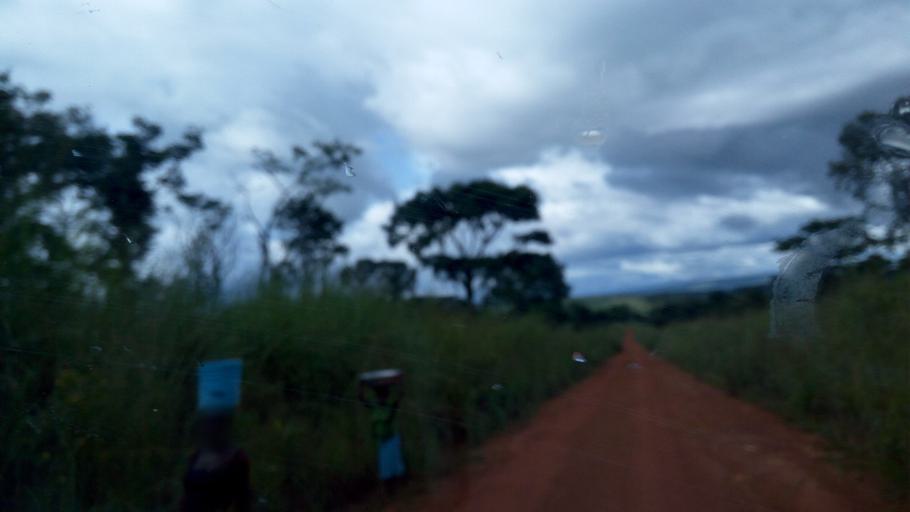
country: ZM
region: Northern
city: Kaputa
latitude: -7.8327
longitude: 29.1731
